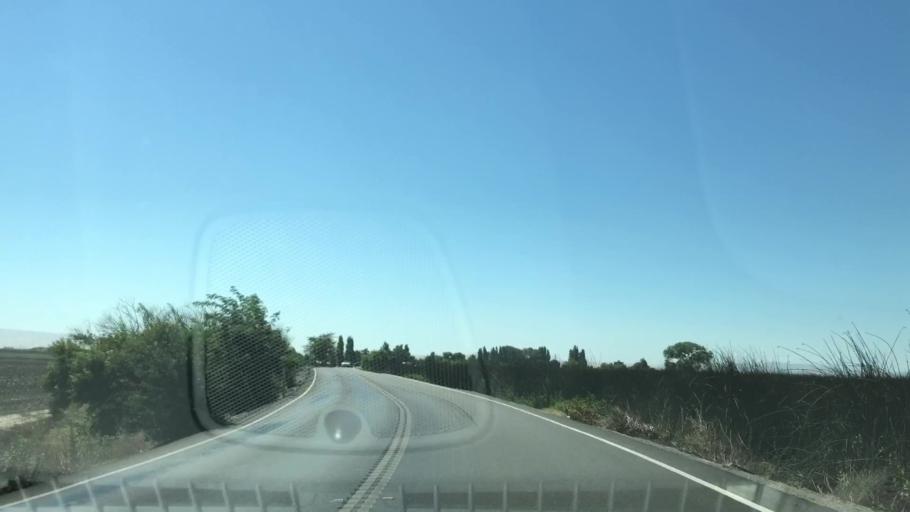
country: US
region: California
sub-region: Contra Costa County
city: Discovery Bay
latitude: 37.8964
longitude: -121.4817
